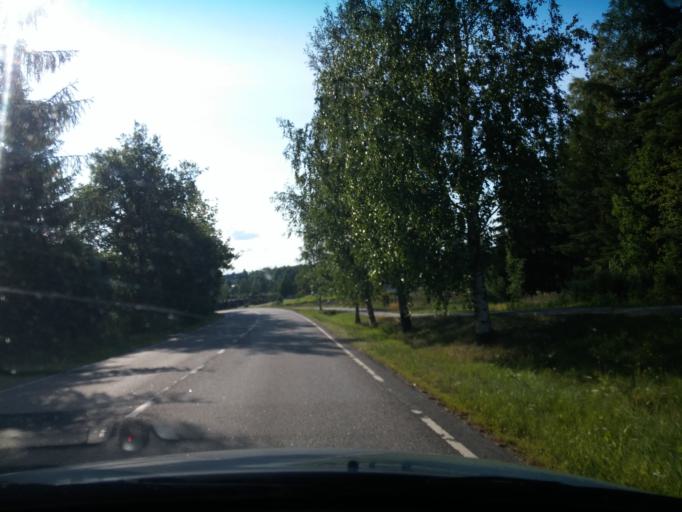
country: FI
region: Uusimaa
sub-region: Porvoo
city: Askola
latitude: 60.4953
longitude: 25.5486
